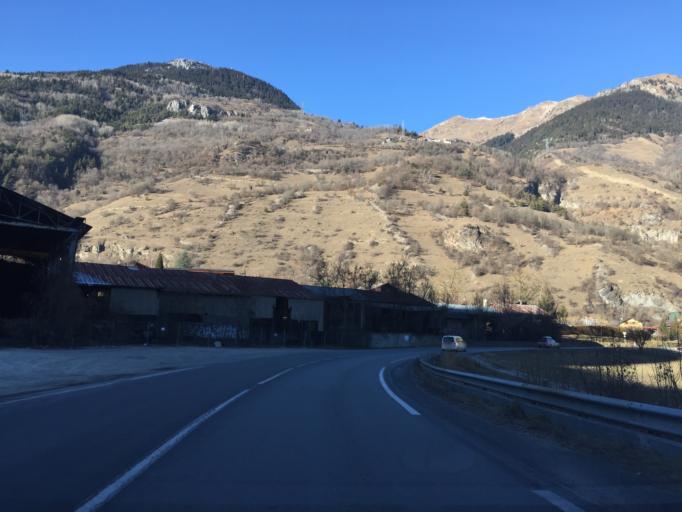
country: FR
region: Rhone-Alpes
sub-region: Departement de la Savoie
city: Aime
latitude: 45.5465
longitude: 6.6156
